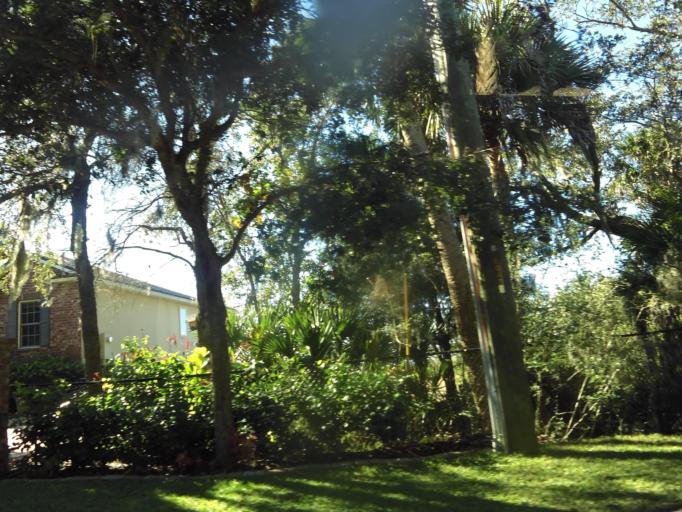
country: US
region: Florida
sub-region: Duval County
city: Atlantic Beach
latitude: 30.4039
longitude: -81.4325
